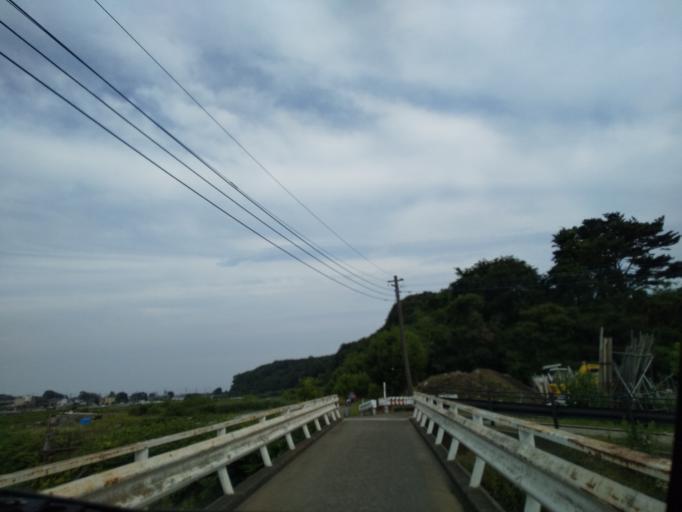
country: JP
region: Kanagawa
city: Atsugi
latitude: 35.4829
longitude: 139.3270
